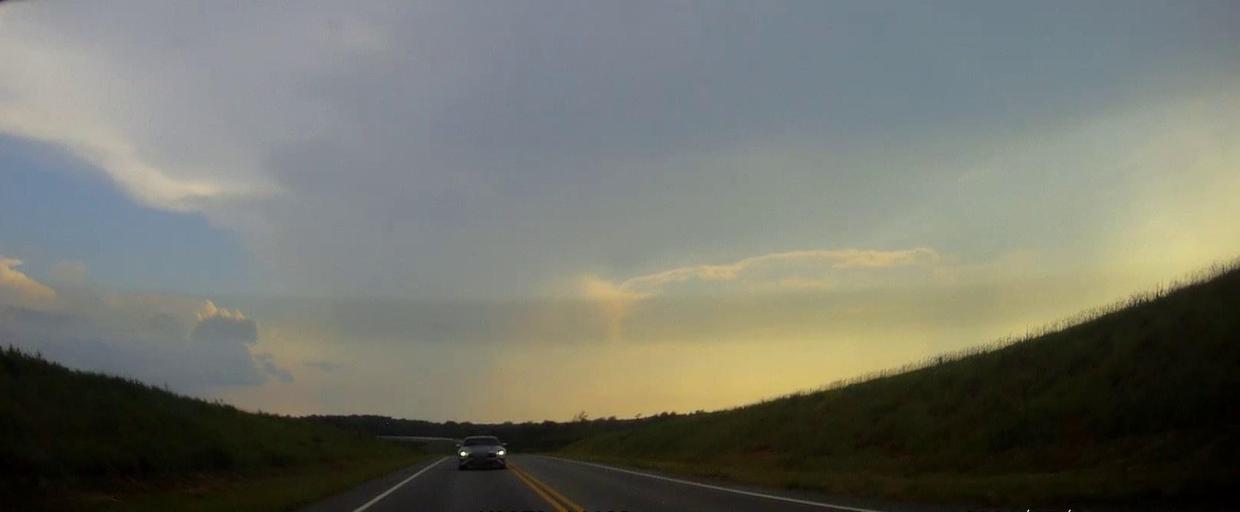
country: US
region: Georgia
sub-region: Laurens County
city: East Dublin
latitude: 32.6170
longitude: -82.8874
